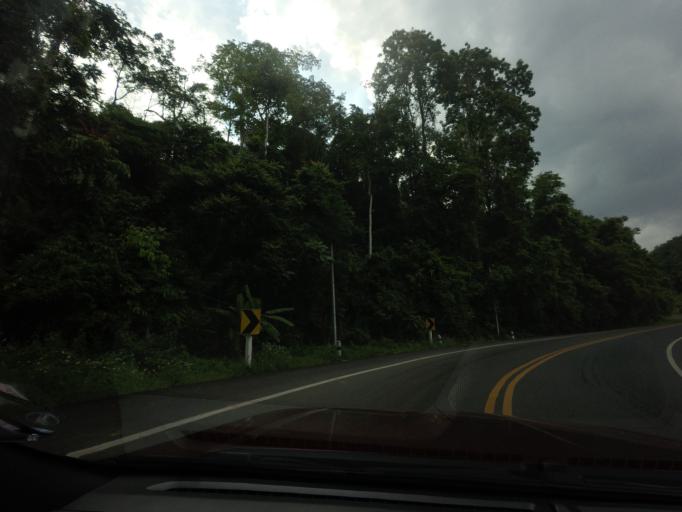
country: TH
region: Yala
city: Than To
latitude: 6.2015
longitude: 101.1713
